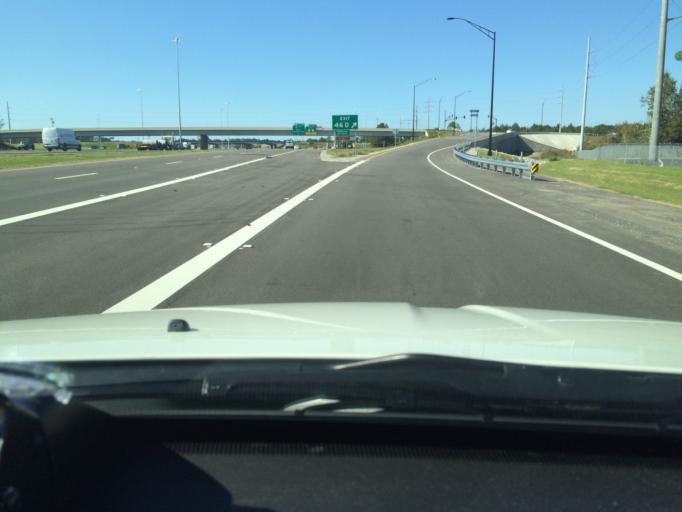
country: US
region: Mississippi
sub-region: Jackson County
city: Saint Martin
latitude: 30.4542
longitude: -88.8888
